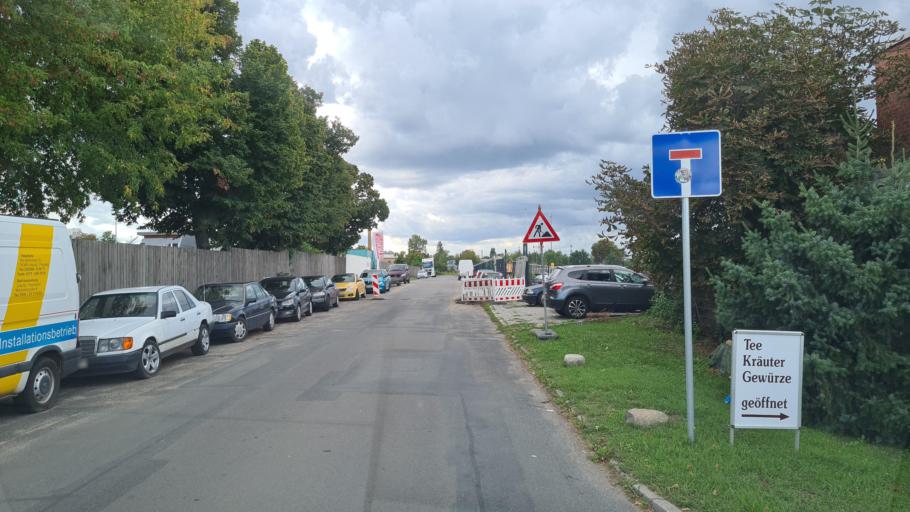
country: DE
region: Saxony
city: Taucha
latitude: 51.3796
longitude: 12.4808
